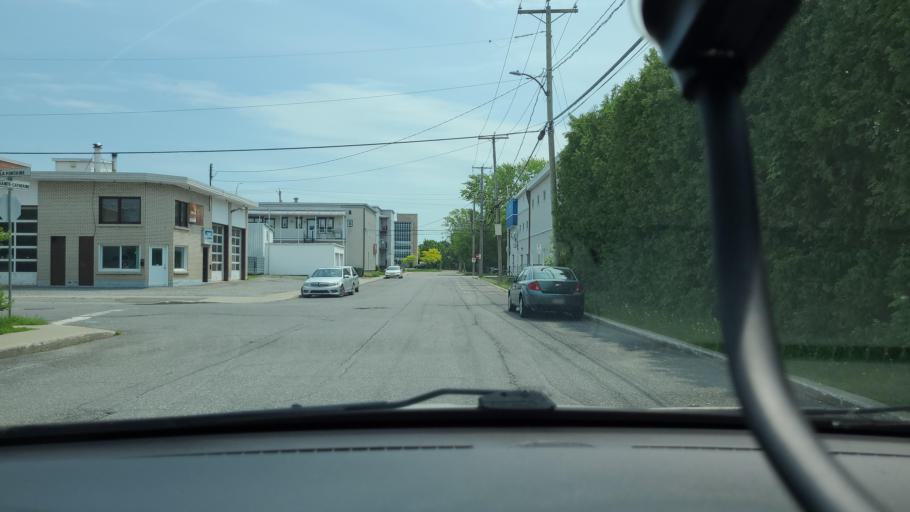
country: CA
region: Quebec
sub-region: Monteregie
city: Saint-Hyacinthe
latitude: 45.6234
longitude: -72.9563
